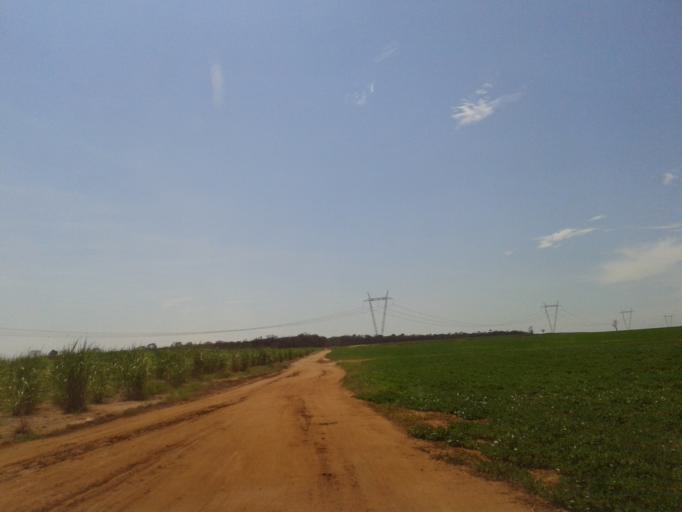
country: BR
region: Minas Gerais
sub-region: Santa Vitoria
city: Santa Vitoria
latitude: -19.0651
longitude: -50.4686
